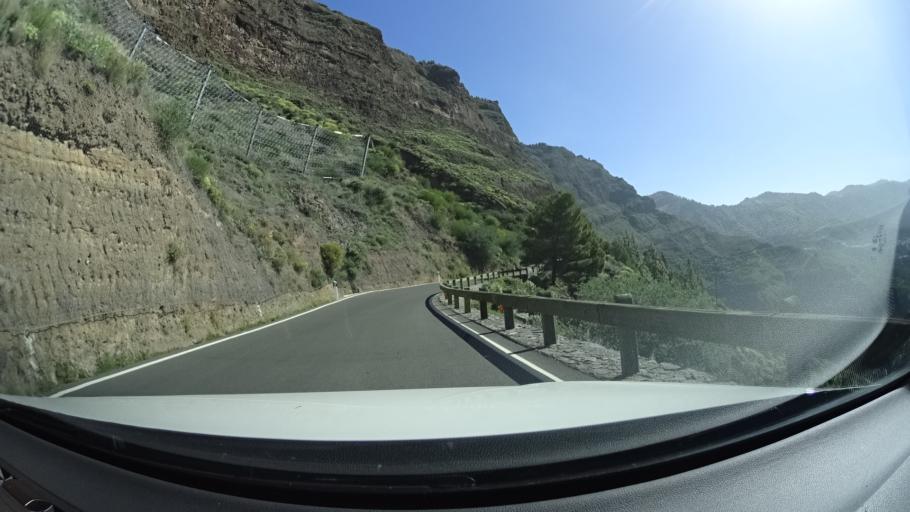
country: ES
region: Canary Islands
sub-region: Provincia de Las Palmas
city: Artenara
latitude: 28.0161
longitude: -15.6370
